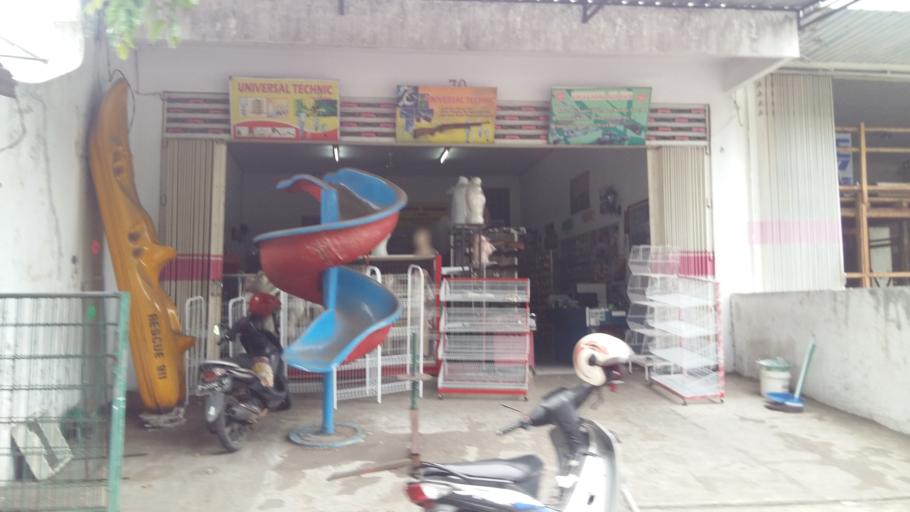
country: ID
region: East Java
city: Krajan
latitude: -8.3102
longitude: 114.2920
